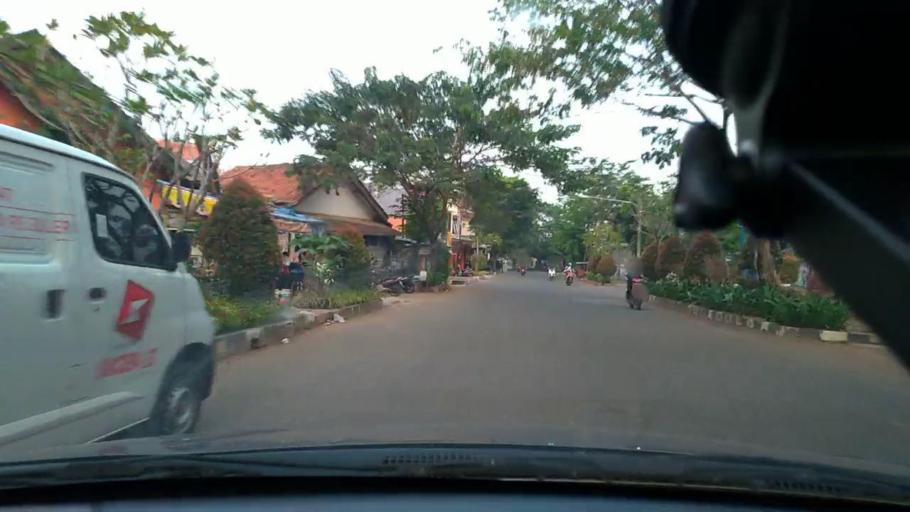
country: ID
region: West Java
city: Purwakarta
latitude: -6.5328
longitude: 107.4404
